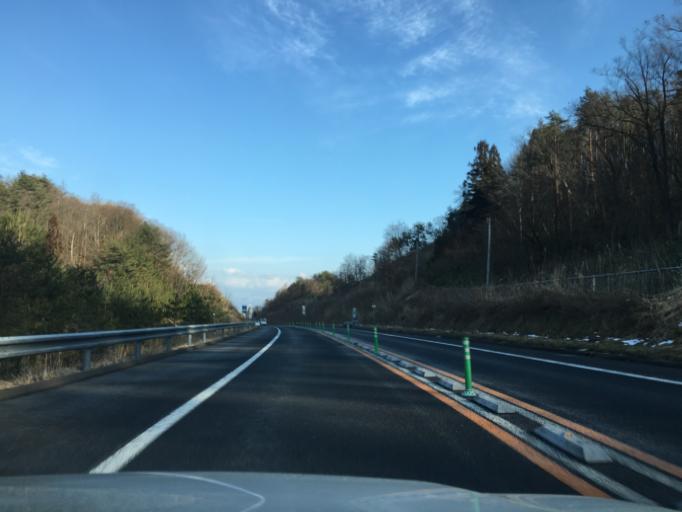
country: JP
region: Yamagata
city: Sagae
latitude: 38.4037
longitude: 140.1960
